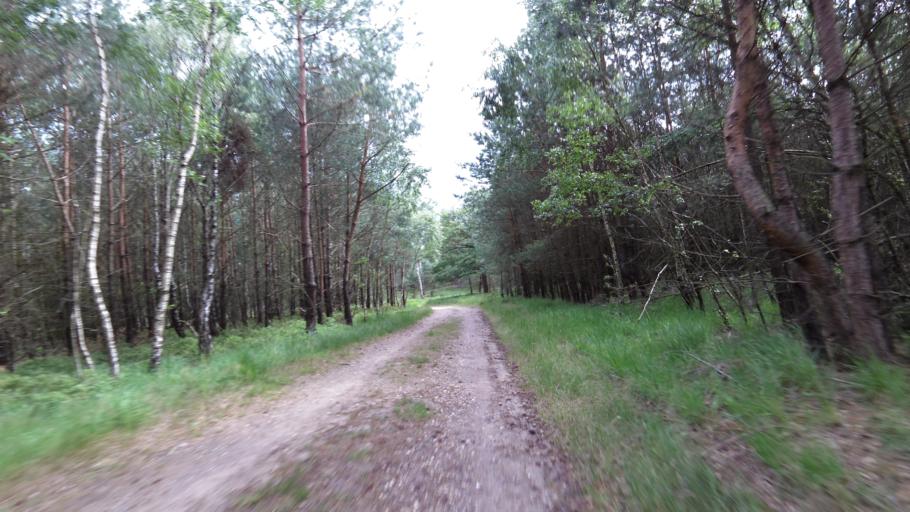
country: NL
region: Gelderland
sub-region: Gemeente Apeldoorn
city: Apeldoorn
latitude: 52.2115
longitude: 5.8833
